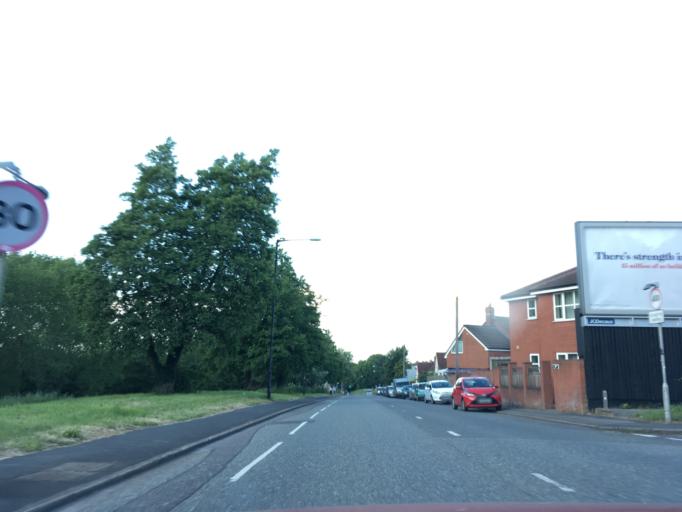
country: GB
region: England
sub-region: Bristol
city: Bristol
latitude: 51.4275
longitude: -2.6166
